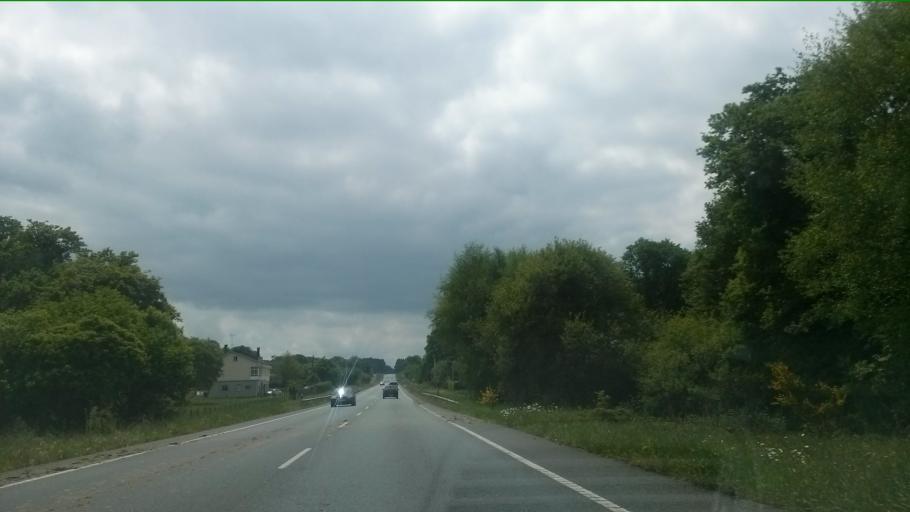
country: ES
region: Galicia
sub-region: Provincia da Coruna
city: Curtis
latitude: 43.1323
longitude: -8.0413
